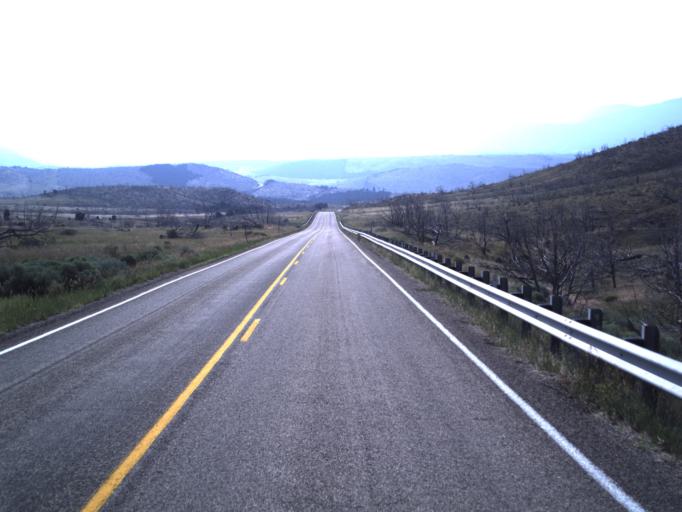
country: US
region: Utah
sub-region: Daggett County
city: Manila
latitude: 40.9519
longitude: -109.4487
